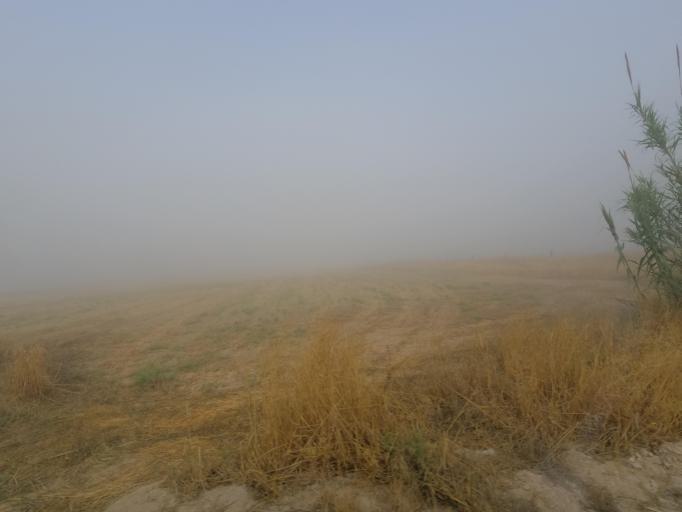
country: CY
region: Ammochostos
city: Acheritou
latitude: 35.0922
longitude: 33.8762
